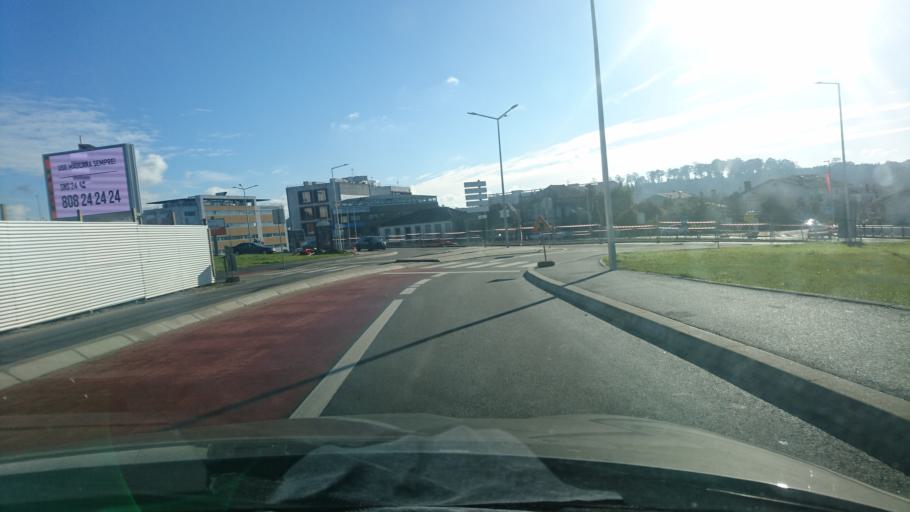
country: PT
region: Aveiro
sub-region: Santa Maria da Feira
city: Feira
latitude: 40.9291
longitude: -8.5485
